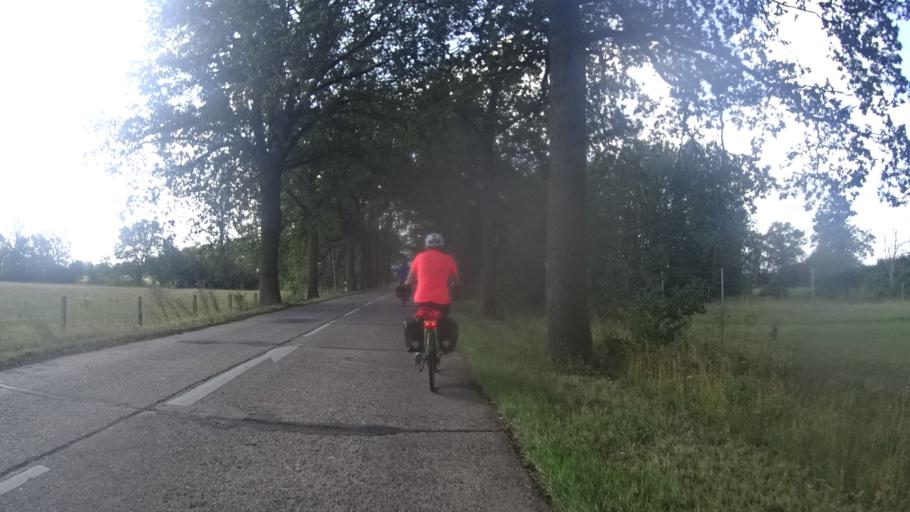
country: DE
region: Brandenburg
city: Ruhstadt
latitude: 52.9302
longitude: 11.8667
